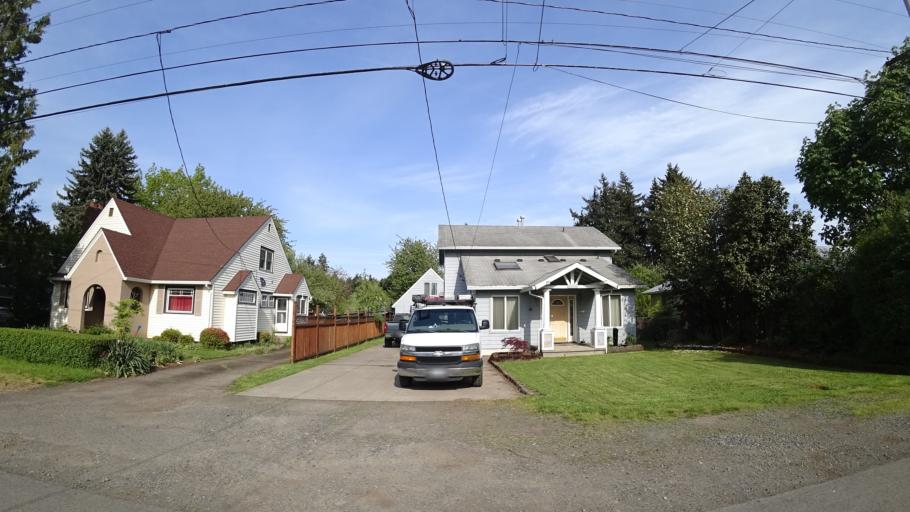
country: US
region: Oregon
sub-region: Clackamas County
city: Milwaukie
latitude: 45.4735
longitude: -122.6134
